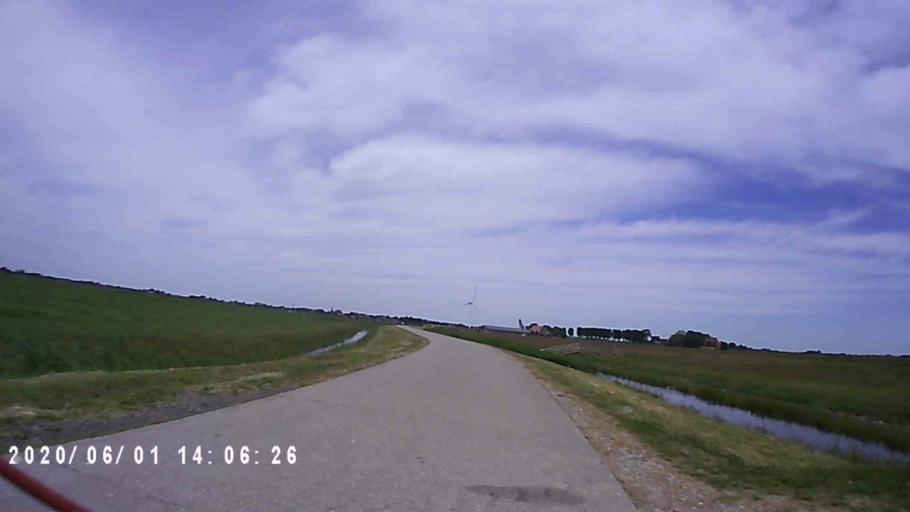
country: NL
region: Friesland
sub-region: Gemeente Littenseradiel
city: Winsum
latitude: 53.1176
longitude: 5.6405
